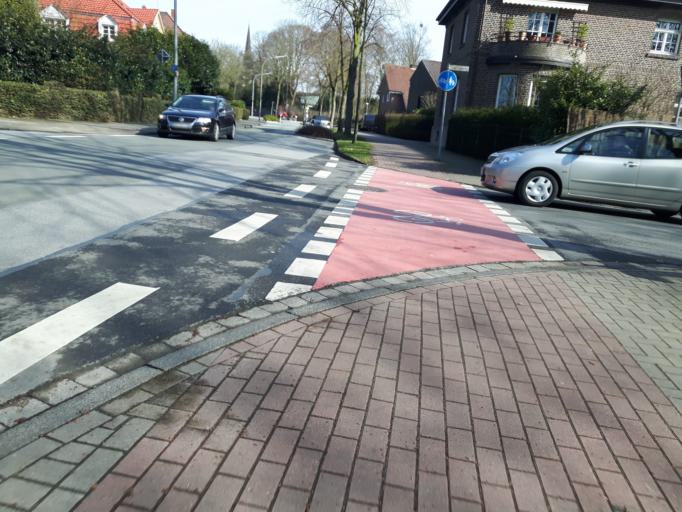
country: DE
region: North Rhine-Westphalia
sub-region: Regierungsbezirk Munster
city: Dulmen
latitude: 51.8242
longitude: 7.2767
